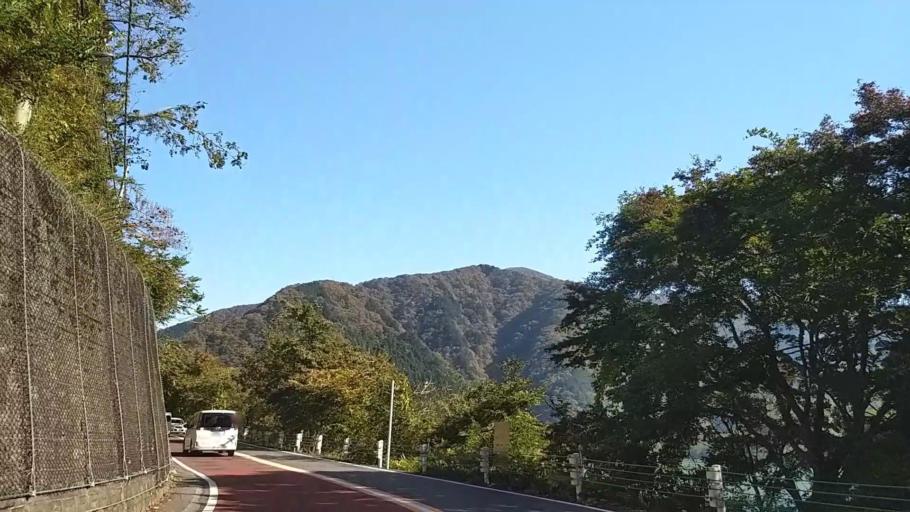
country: JP
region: Tokyo
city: Itsukaichi
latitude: 35.7867
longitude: 139.0430
